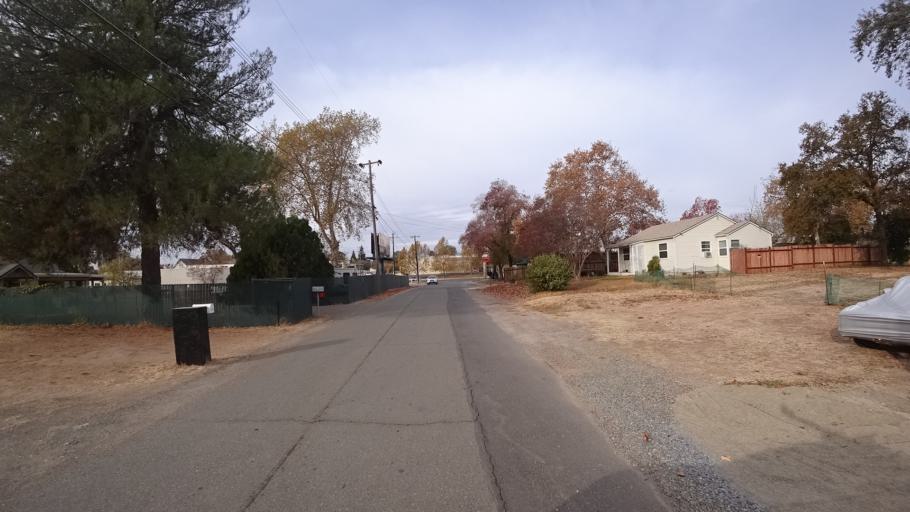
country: US
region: California
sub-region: Sacramento County
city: Citrus Heights
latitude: 38.7203
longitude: -121.2891
